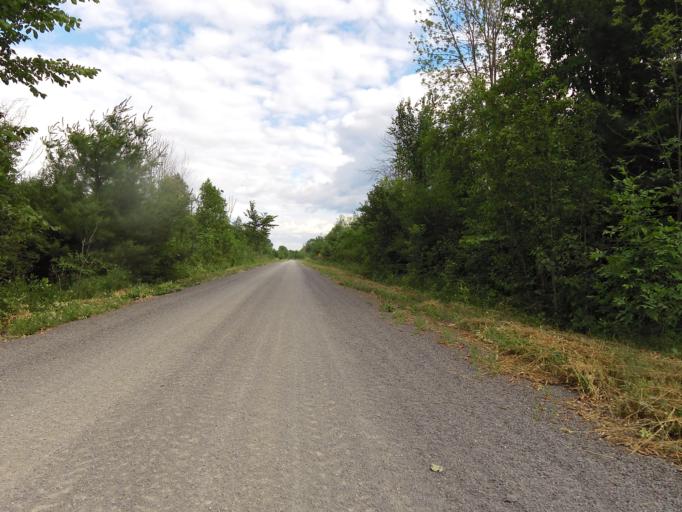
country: CA
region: Ontario
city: Arnprior
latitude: 45.2888
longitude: -76.2531
